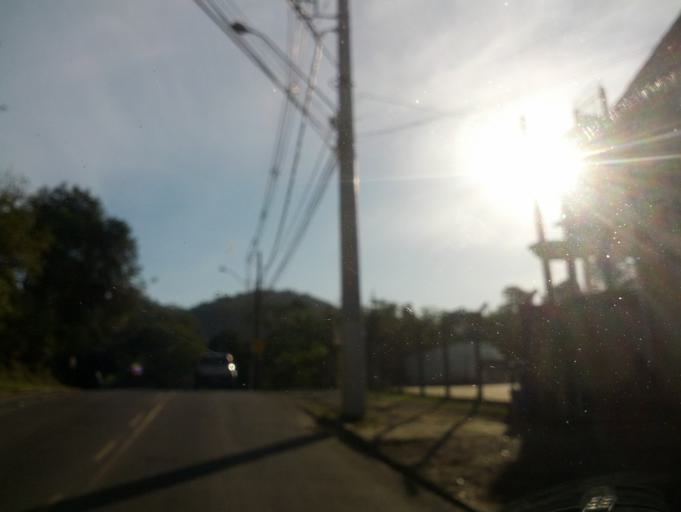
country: BR
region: Santa Catarina
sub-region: Blumenau
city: Blumenau
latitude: -26.9087
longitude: -49.1452
